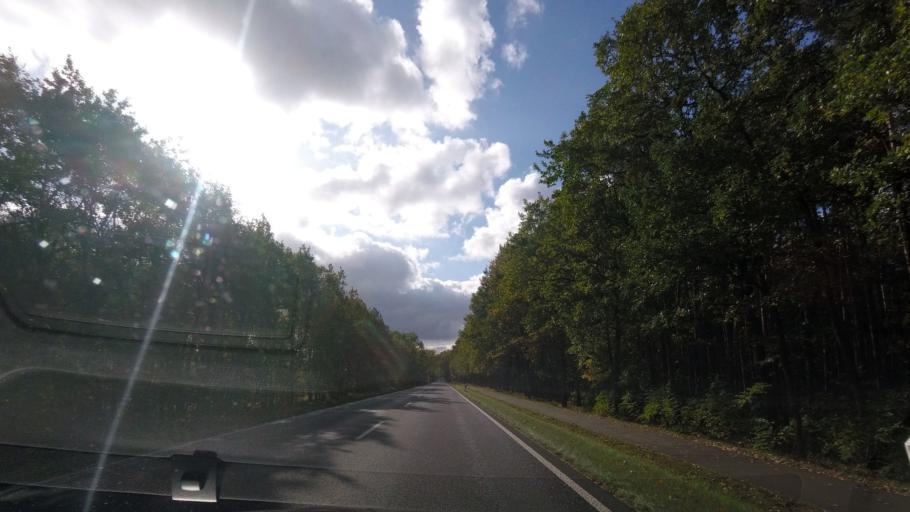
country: DE
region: Brandenburg
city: Treuenbrietzen
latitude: 52.1117
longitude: 12.8876
